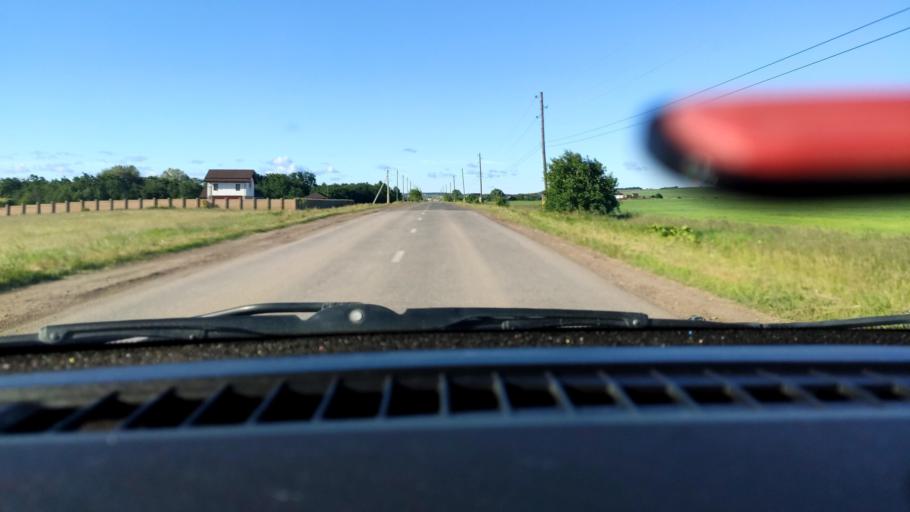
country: RU
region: Perm
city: Kultayevo
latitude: 57.8786
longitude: 55.9224
